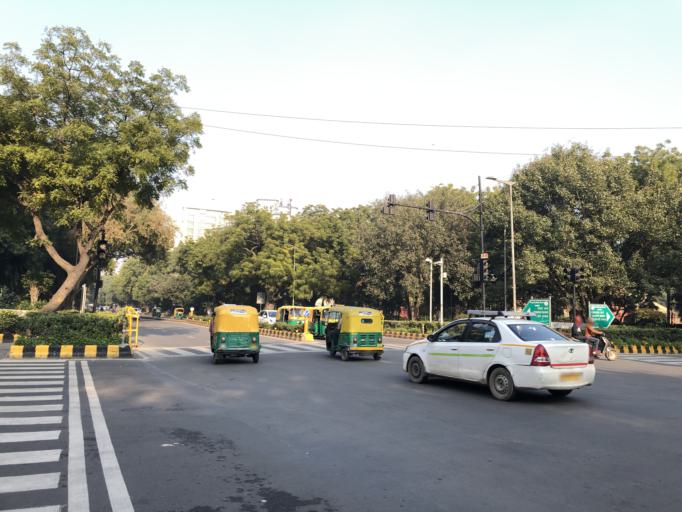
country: IN
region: NCT
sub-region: New Delhi
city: New Delhi
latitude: 28.6270
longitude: 77.2153
